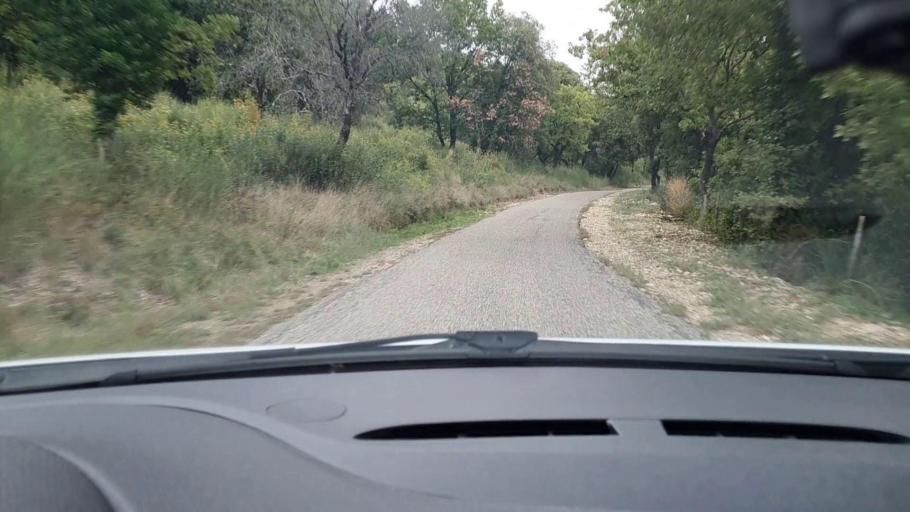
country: FR
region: Languedoc-Roussillon
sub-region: Departement du Gard
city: Mons
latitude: 44.1374
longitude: 4.2887
